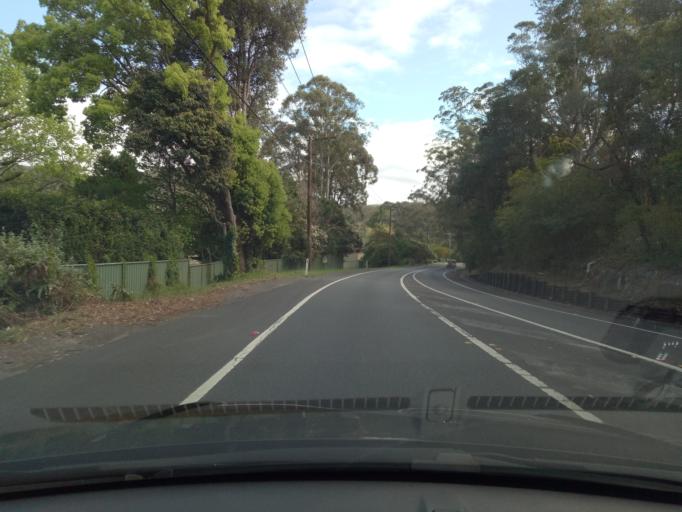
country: AU
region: New South Wales
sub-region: Gosford Shire
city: Lisarow
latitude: -33.3873
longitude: 151.3545
